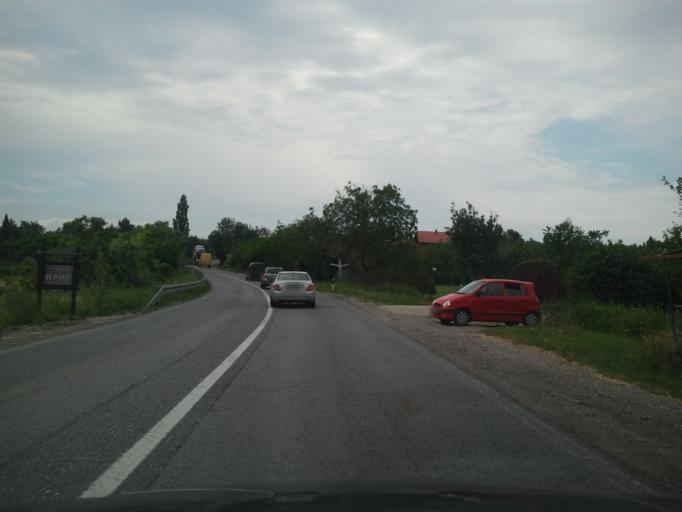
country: RS
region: Autonomna Pokrajina Vojvodina
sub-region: Sremski Okrug
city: Irig
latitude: 45.1213
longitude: 19.8477
